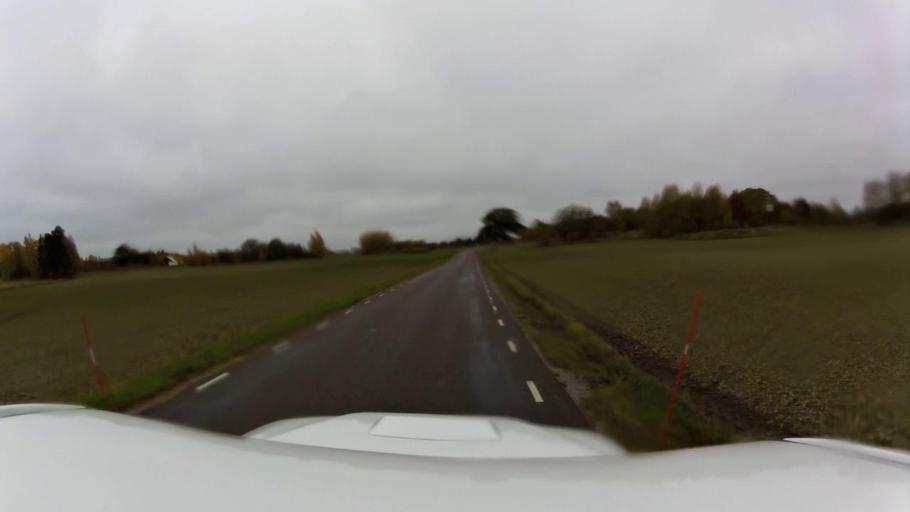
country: SE
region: OEstergoetland
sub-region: Linkopings Kommun
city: Linghem
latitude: 58.4732
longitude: 15.7219
